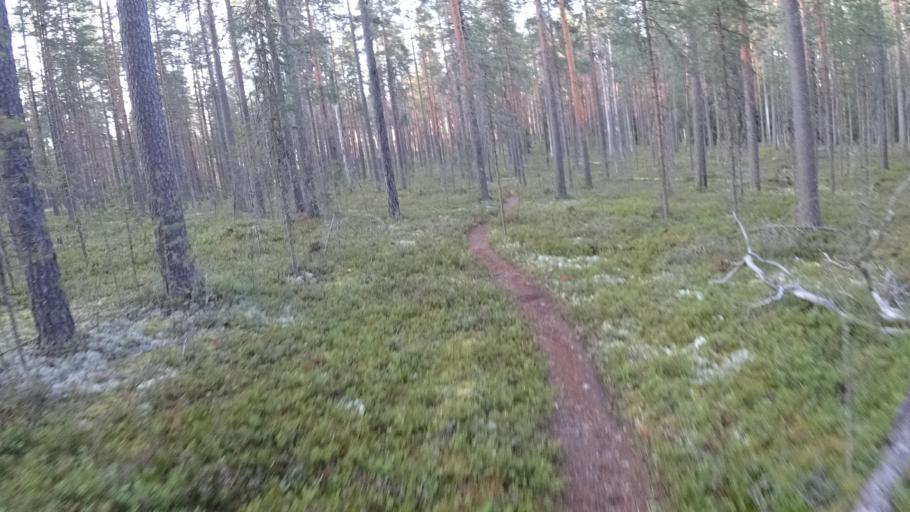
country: FI
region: North Karelia
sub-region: Joensuu
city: Ilomantsi
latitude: 62.5828
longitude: 31.1842
